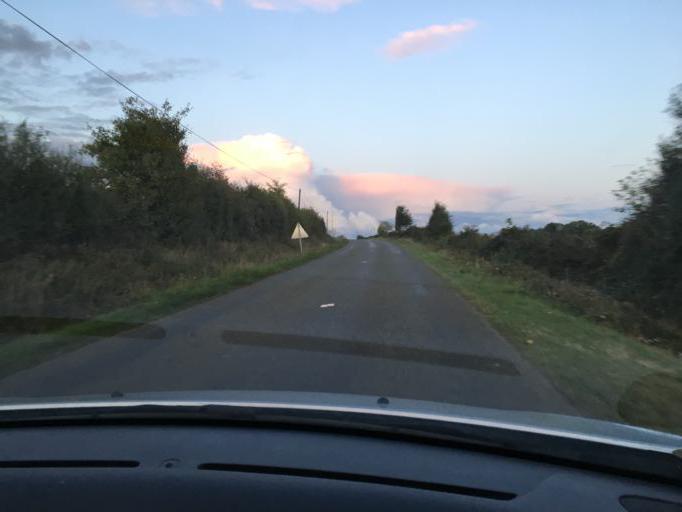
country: FR
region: Centre
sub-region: Departement d'Eure-et-Loir
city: Unverre
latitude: 48.2640
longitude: 1.1010
